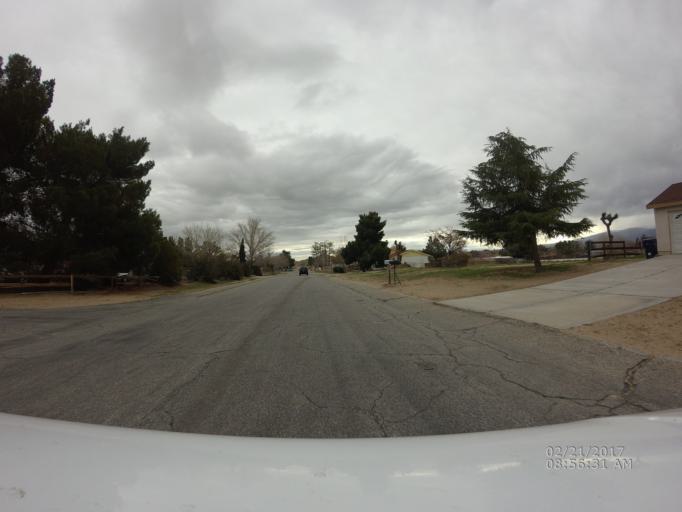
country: US
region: California
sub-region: Los Angeles County
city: Lake Los Angeles
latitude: 34.5954
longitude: -117.8327
